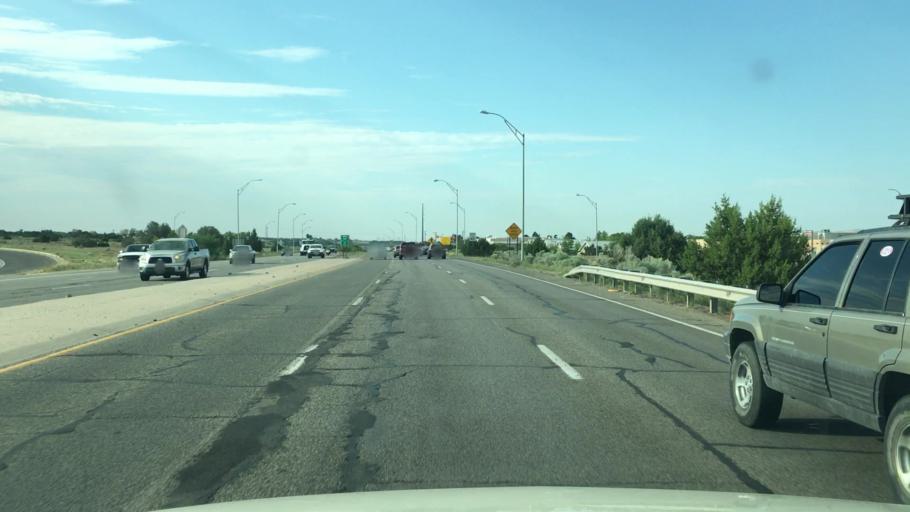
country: US
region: New Mexico
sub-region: Santa Fe County
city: Santa Fe
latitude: 35.6587
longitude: -105.9568
